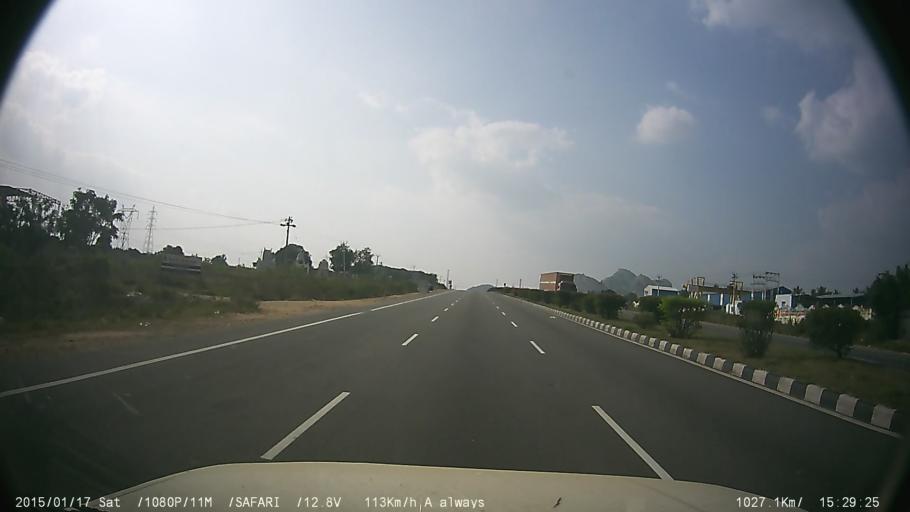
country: IN
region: Tamil Nadu
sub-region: Krishnagiri
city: Kelamangalam
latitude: 12.6484
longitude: 78.0397
